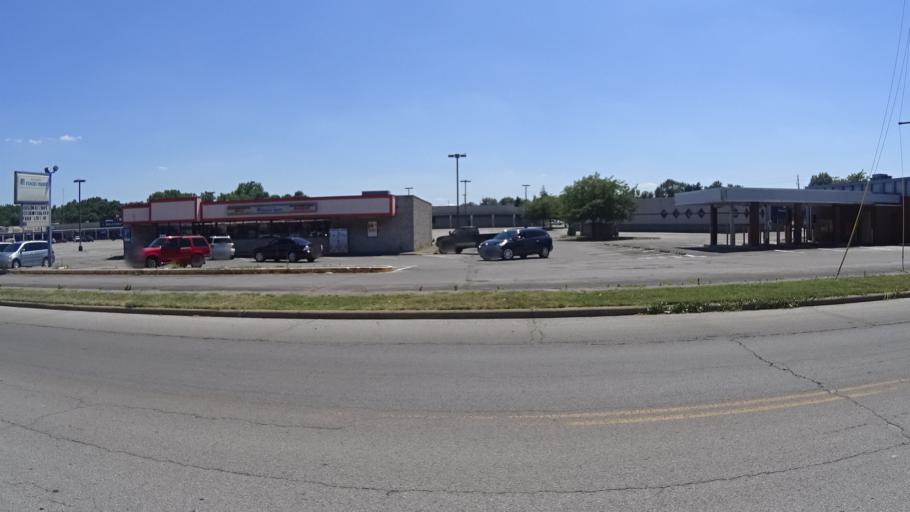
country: US
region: Ohio
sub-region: Erie County
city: Sandusky
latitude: 41.4460
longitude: -82.6958
